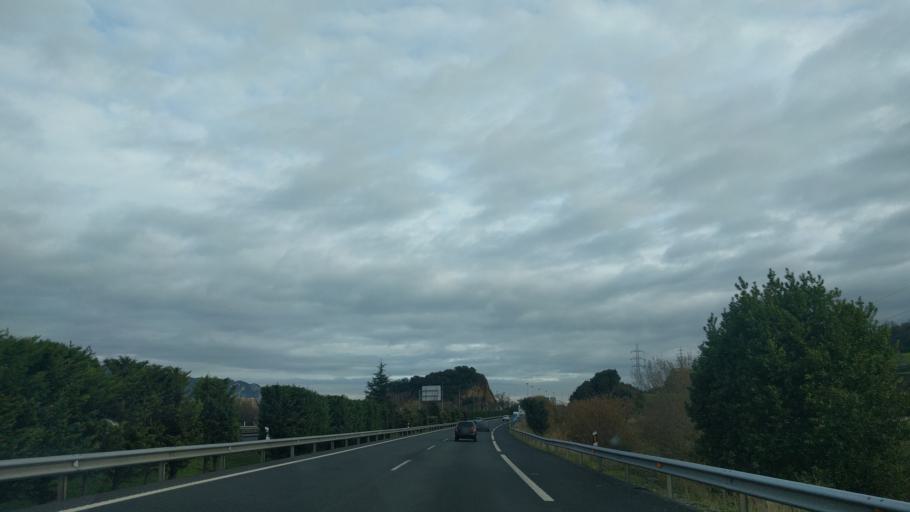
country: ES
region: Cantabria
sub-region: Provincia de Cantabria
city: Colindres
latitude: 43.3953
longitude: -3.4425
